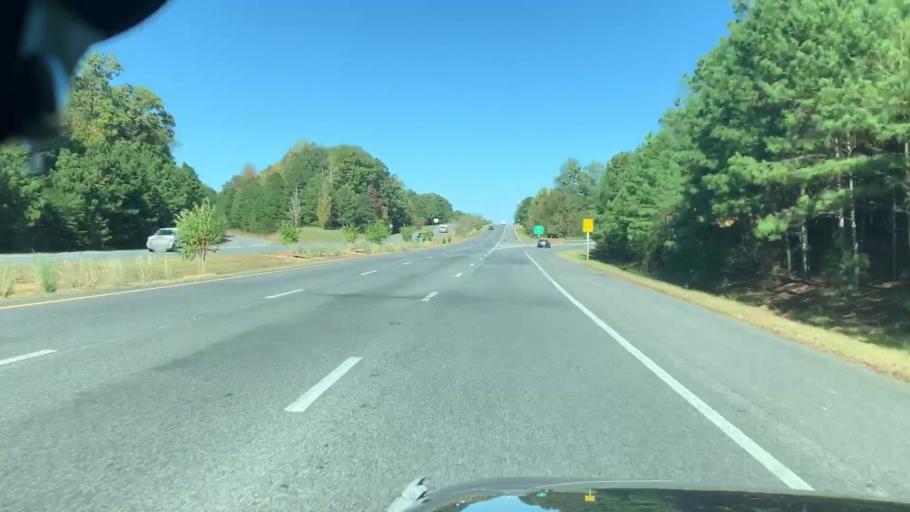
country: US
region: Virginia
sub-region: James City County
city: Williamsburg
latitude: 37.3331
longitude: -76.7536
